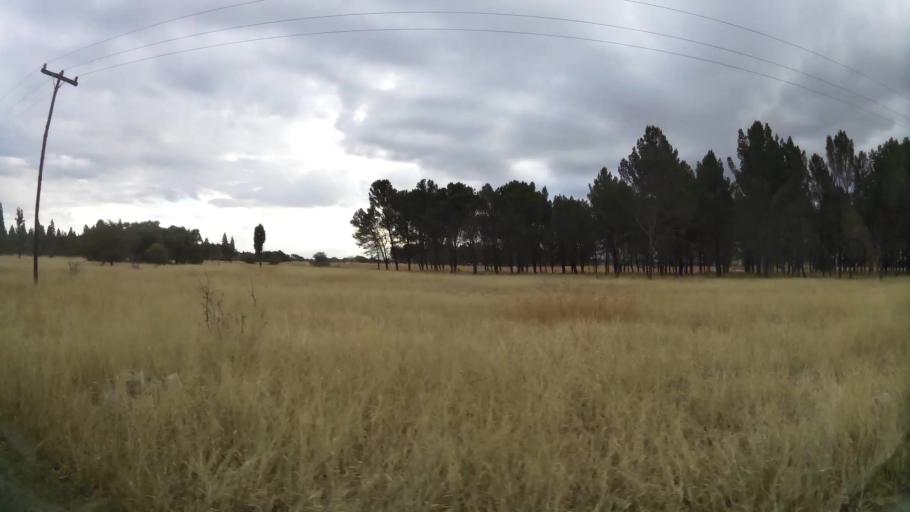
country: ZA
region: Orange Free State
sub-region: Lejweleputswa District Municipality
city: Welkom
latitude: -27.9706
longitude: 26.7008
